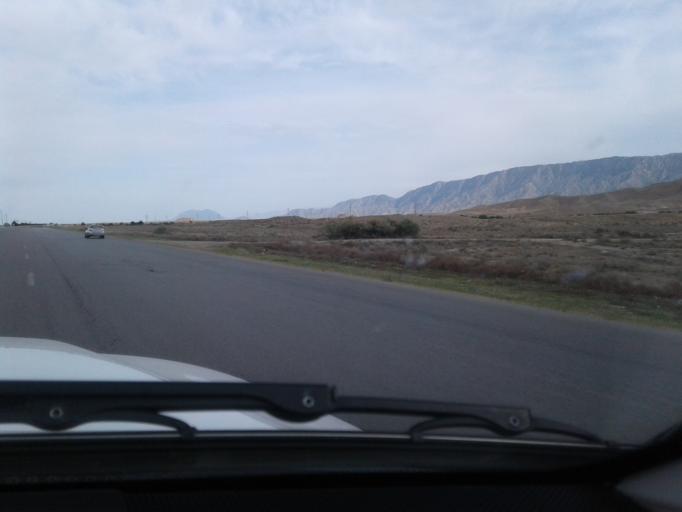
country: TM
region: Ahal
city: Baharly
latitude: 38.2382
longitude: 57.7715
